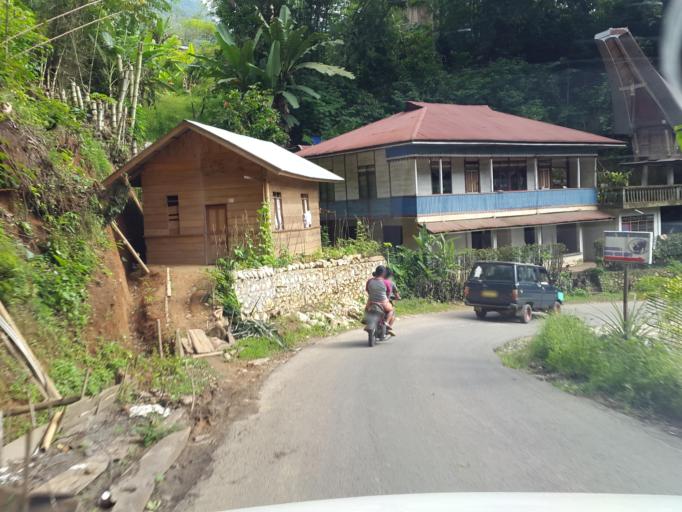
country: ID
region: South Sulawesi
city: Rantepao
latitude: -3.0155
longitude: 119.8648
